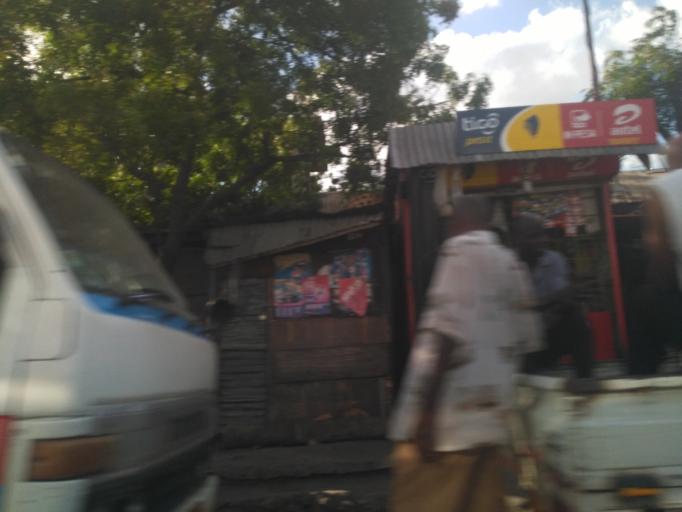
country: TZ
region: Dar es Salaam
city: Dar es Salaam
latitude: -6.8696
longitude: 39.2624
